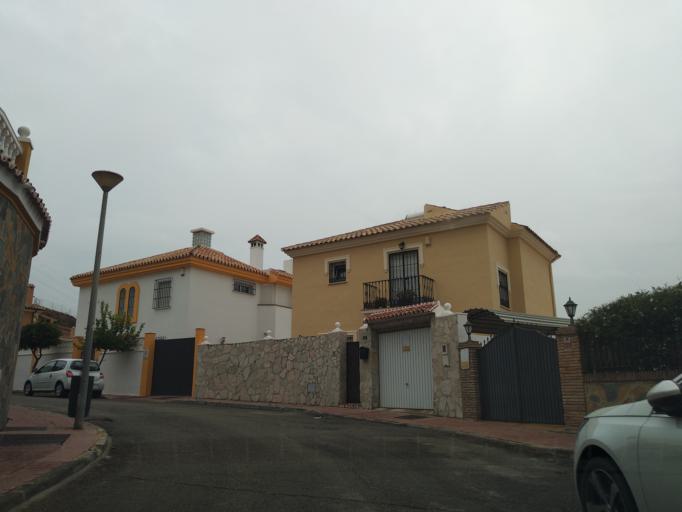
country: ES
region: Andalusia
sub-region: Provincia de Malaga
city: Malaga
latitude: 36.7442
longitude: -4.4751
